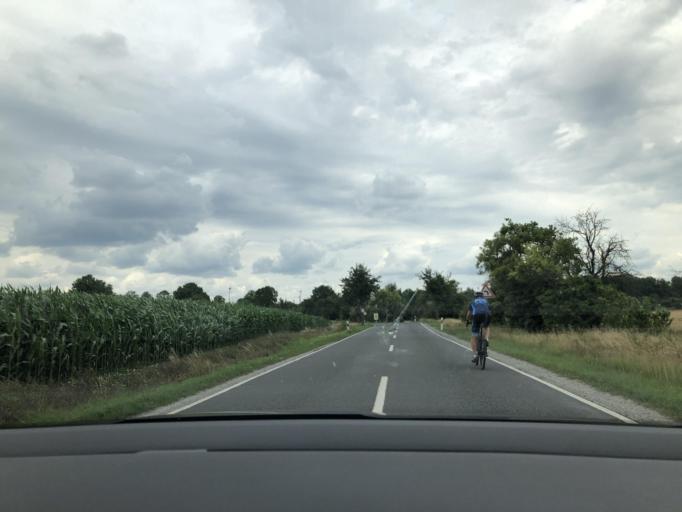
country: DE
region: Saxony-Anhalt
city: Borne
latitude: 51.9431
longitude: 11.5493
